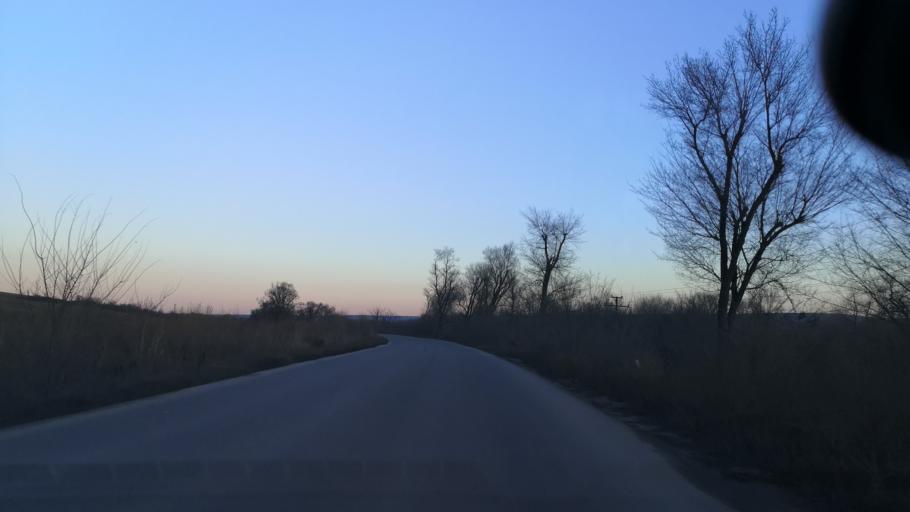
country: MD
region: Anenii Noi
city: Anenii Noi
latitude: 46.8891
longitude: 29.2484
